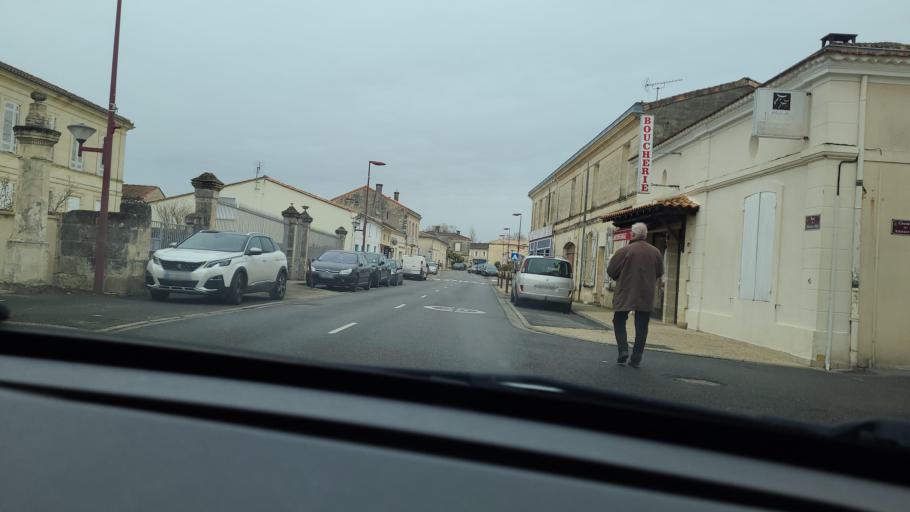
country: FR
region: Aquitaine
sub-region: Departement de la Gironde
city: Pugnac
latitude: 45.0813
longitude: -0.4975
